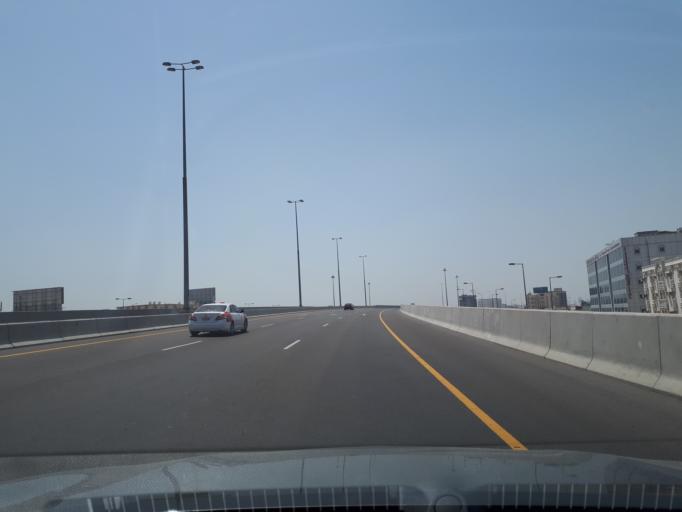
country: OM
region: Al Batinah
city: Al Liwa'
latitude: 24.4227
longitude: 56.6141
